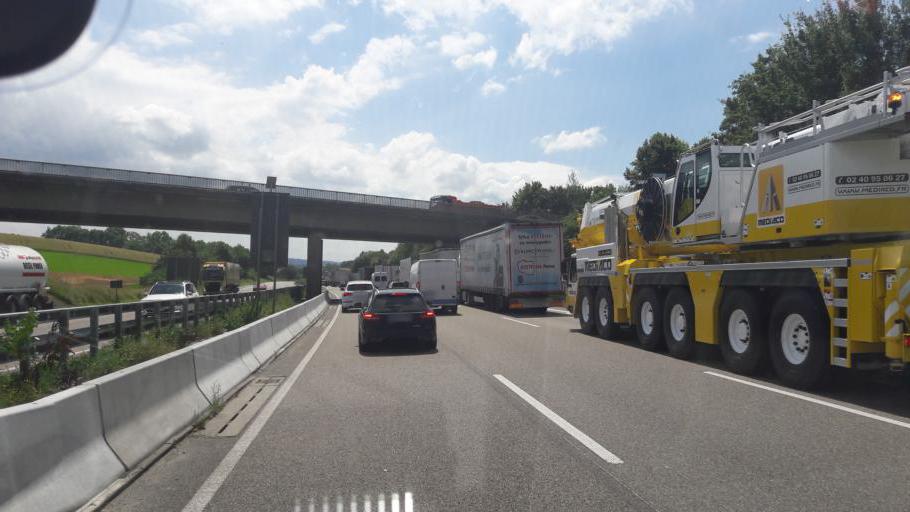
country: DE
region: Baden-Wuerttemberg
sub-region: Regierungsbezirk Stuttgart
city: Bretzfeld
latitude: 49.1874
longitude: 9.4166
